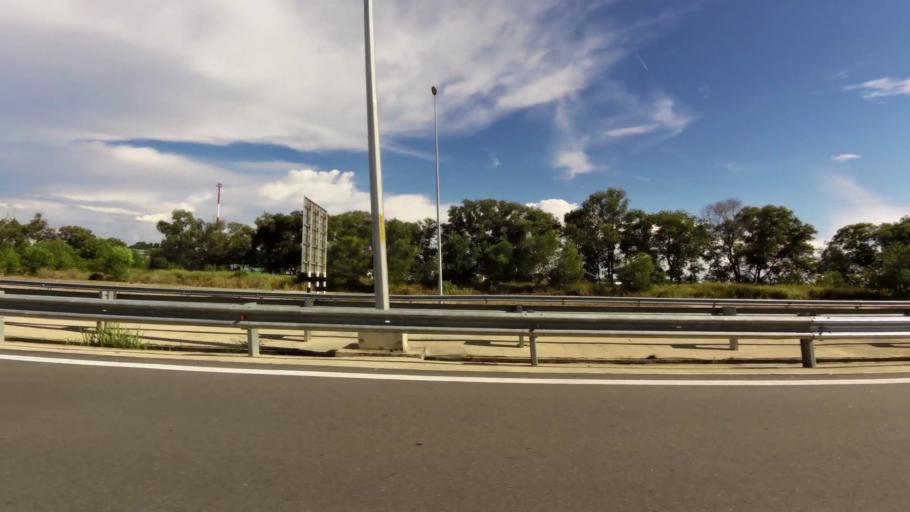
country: BN
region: Brunei and Muara
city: Bandar Seri Begawan
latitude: 4.9865
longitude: 114.9572
